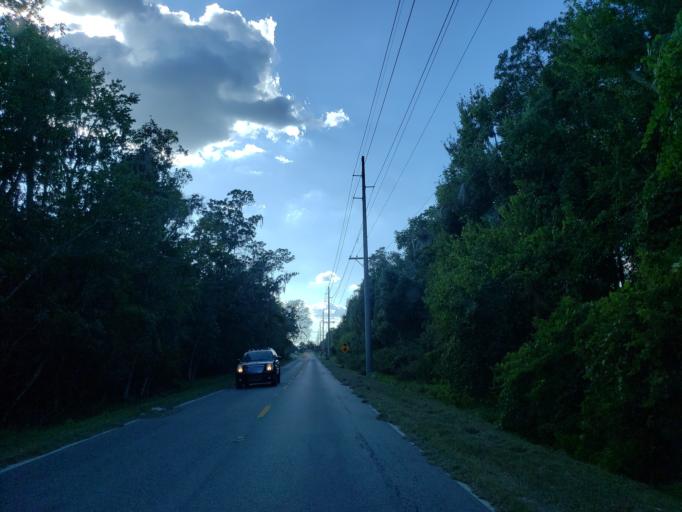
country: US
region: Florida
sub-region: Hillsborough County
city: Dover
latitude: 27.9670
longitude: -82.2174
